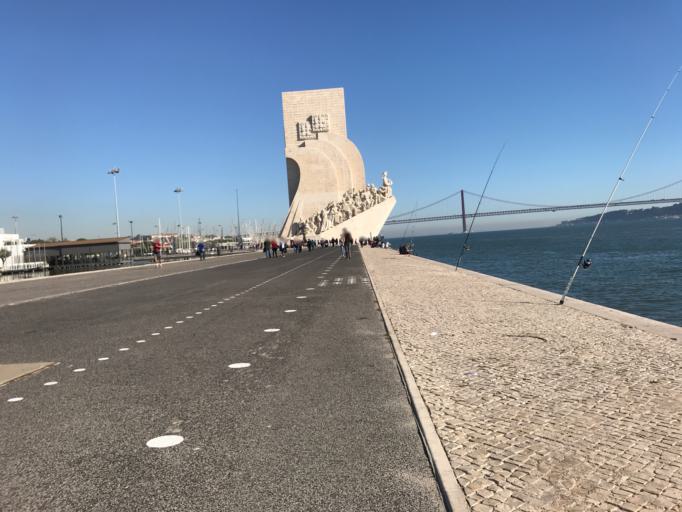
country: PT
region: Lisbon
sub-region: Oeiras
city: Alges
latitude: 38.6932
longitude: -9.2077
